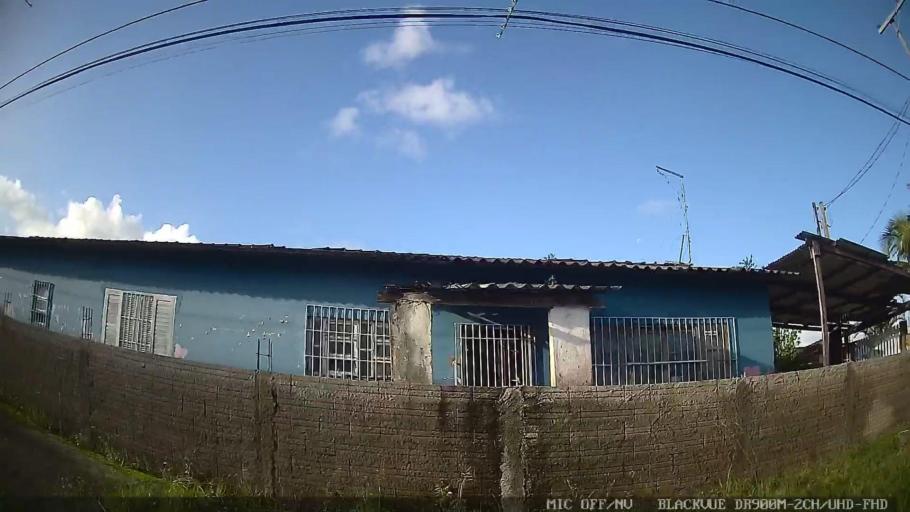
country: BR
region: Sao Paulo
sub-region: Itanhaem
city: Itanhaem
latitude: -24.1398
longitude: -46.7147
